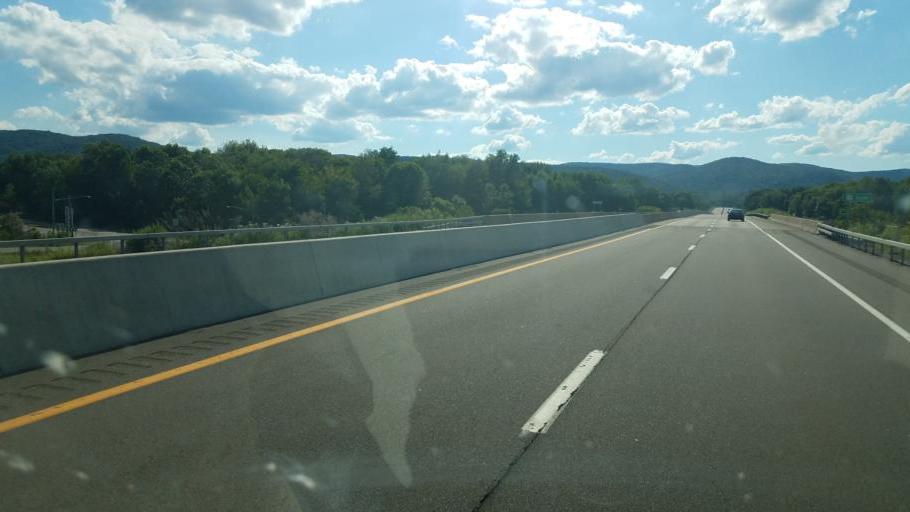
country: US
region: New York
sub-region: Cattaraugus County
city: Salamanca
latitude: 42.0881
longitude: -78.6296
